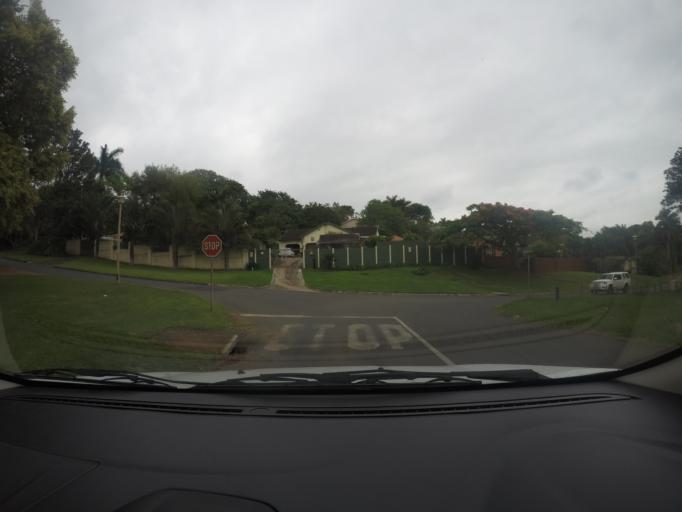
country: ZA
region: KwaZulu-Natal
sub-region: uThungulu District Municipality
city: Empangeni
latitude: -28.7580
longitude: 31.8902
